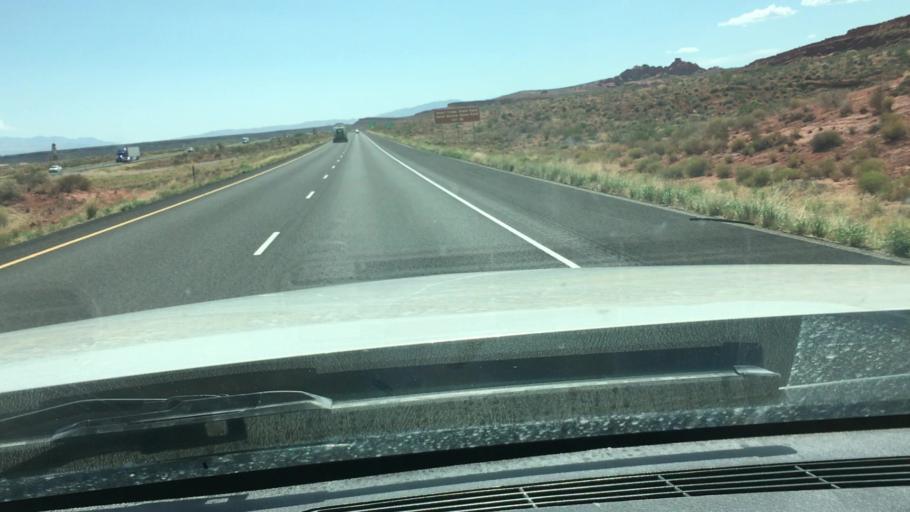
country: US
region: Utah
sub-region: Washington County
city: Washington
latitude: 37.1729
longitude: -113.4377
